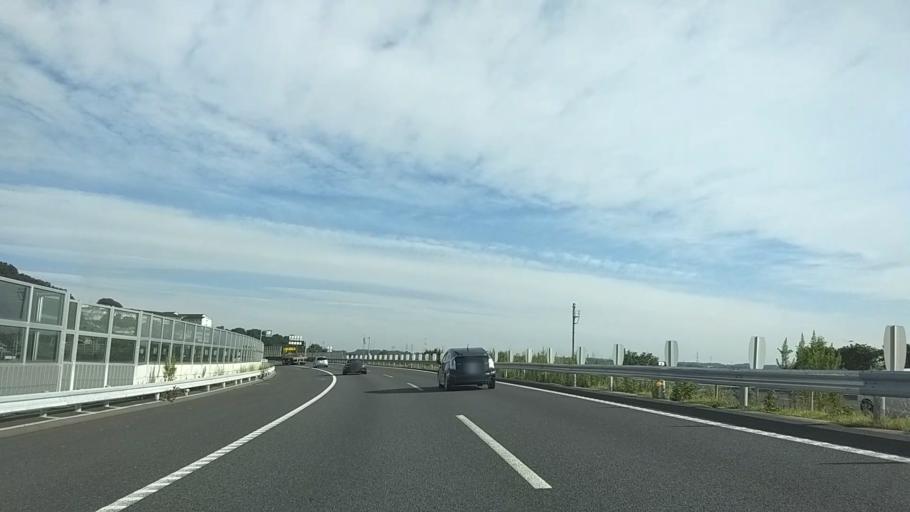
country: JP
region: Kanagawa
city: Zama
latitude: 35.5054
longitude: 139.3662
